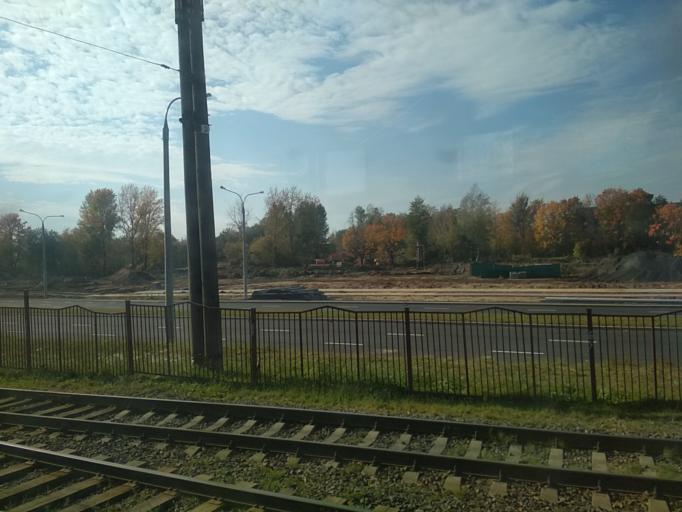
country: BY
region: Minsk
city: Syenitsa
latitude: 53.8607
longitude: 27.5591
